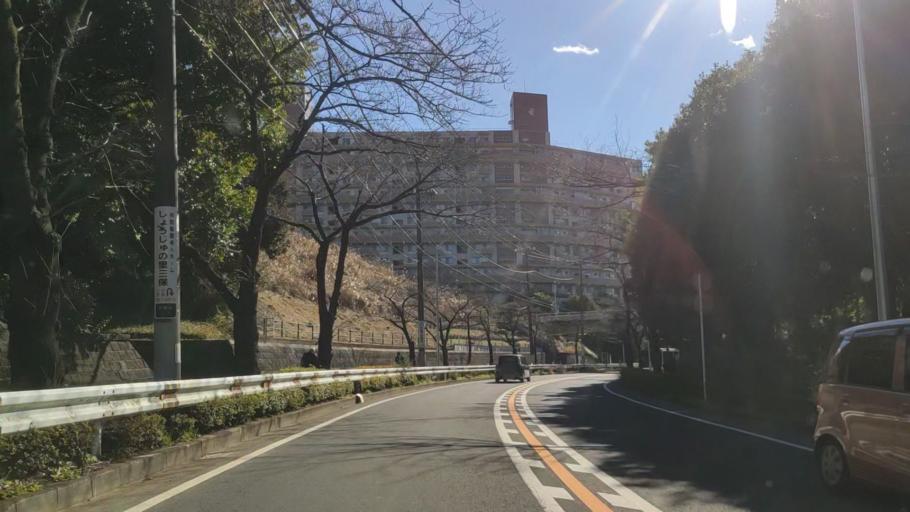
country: JP
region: Kanagawa
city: Minami-rinkan
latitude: 35.5040
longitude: 139.5045
